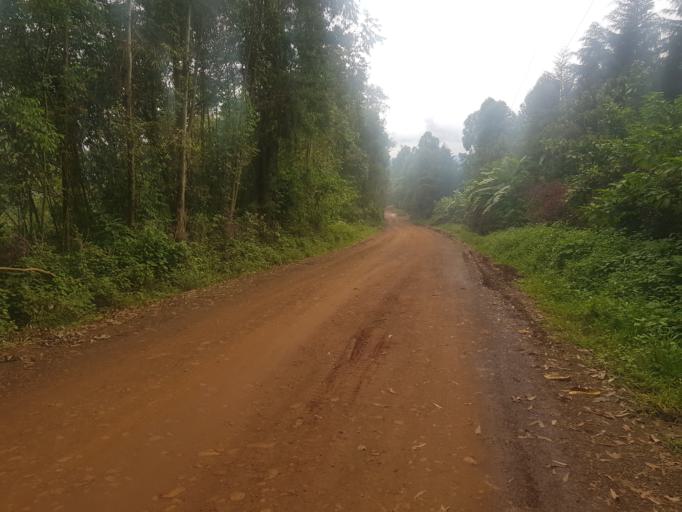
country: ET
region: Oromiya
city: Gore
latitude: 7.8942
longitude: 35.4911
